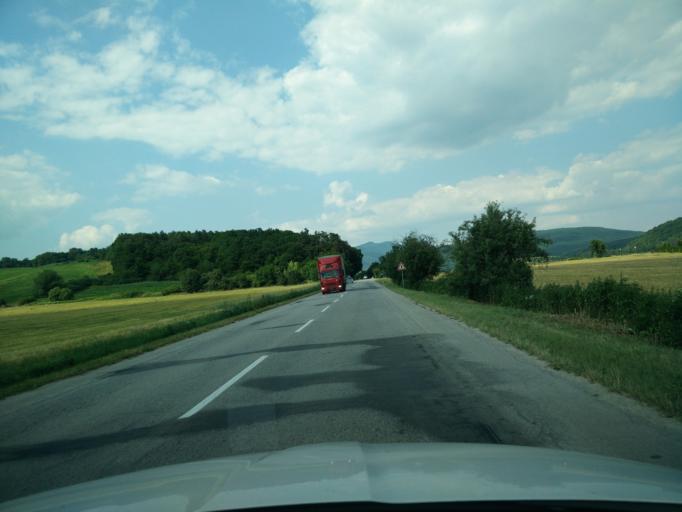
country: SK
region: Nitriansky
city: Partizanske
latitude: 48.6647
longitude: 18.3666
